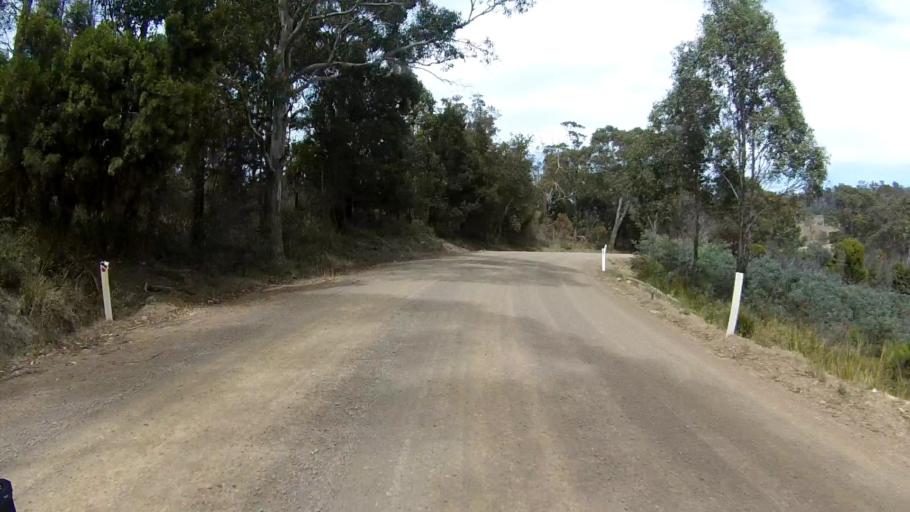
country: AU
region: Tasmania
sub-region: Sorell
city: Sorell
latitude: -42.7959
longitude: 147.6891
